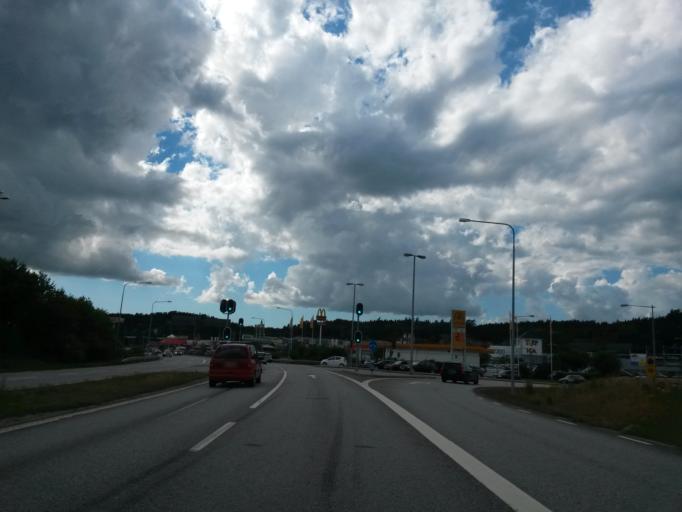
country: SE
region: Vaestra Goetaland
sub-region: Uddevalla Kommun
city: Uddevalla
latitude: 58.3522
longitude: 11.8133
